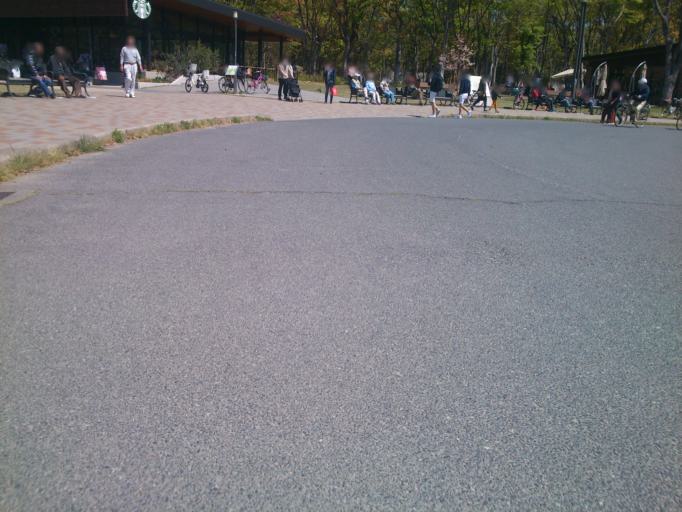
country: JP
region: Osaka
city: Osaka-shi
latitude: 34.6827
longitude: 135.5318
